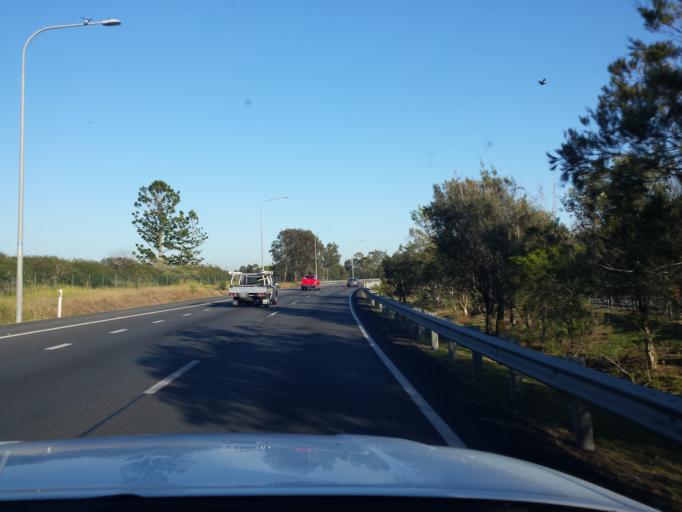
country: AU
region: Queensland
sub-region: Logan
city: Beenleigh
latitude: -27.6836
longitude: 153.1738
